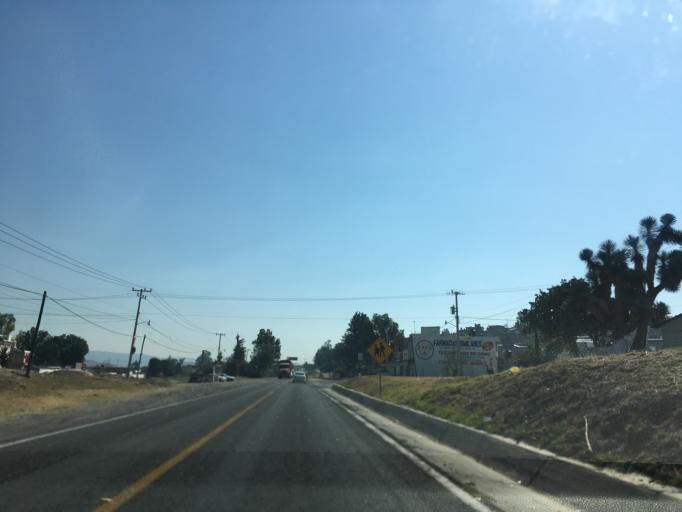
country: MX
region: Michoacan
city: Charo
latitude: 19.7366
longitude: -101.0841
